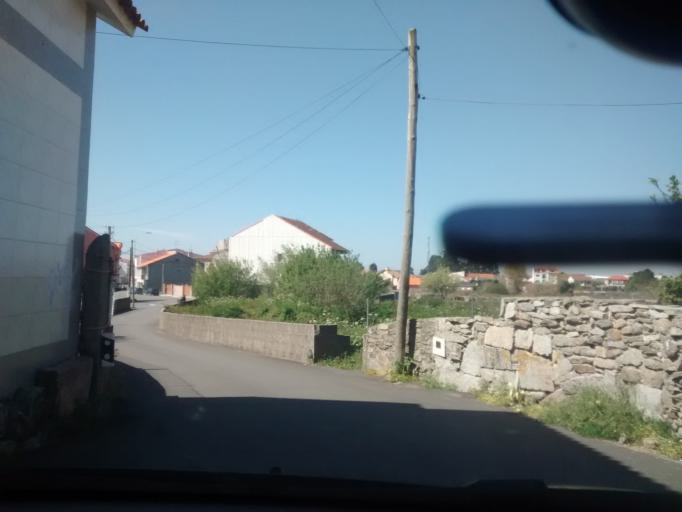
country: ES
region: Galicia
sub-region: Provincia de Pontevedra
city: O Grove
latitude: 42.4925
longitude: -8.8810
